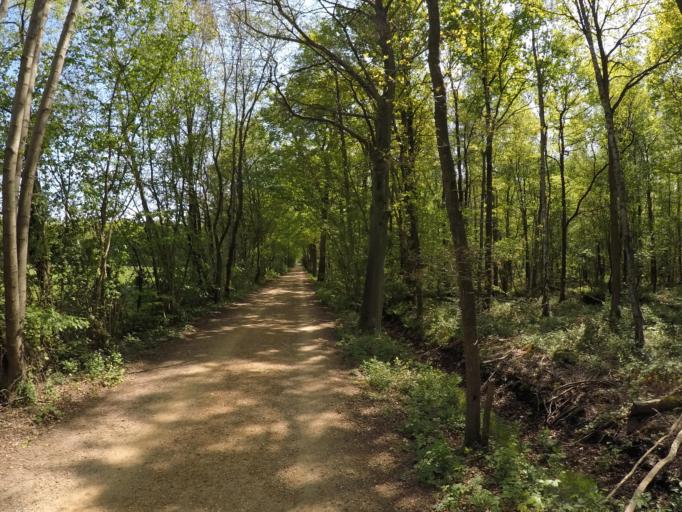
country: BE
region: Flanders
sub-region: Provincie Antwerpen
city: Zoersel
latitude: 51.2586
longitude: 4.6853
